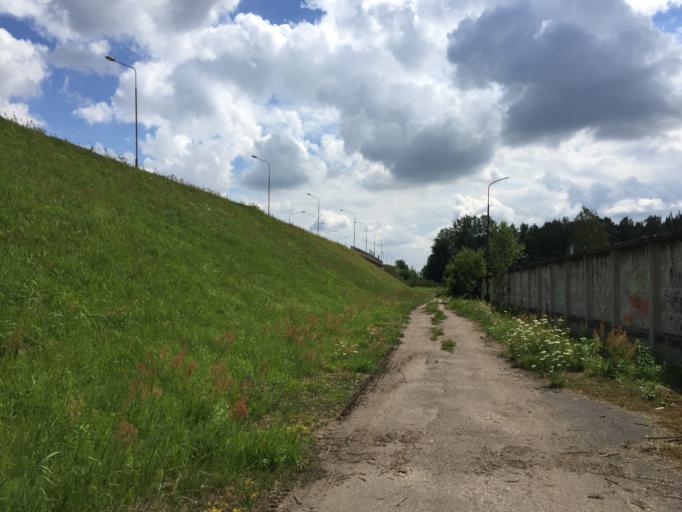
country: LV
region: Ozolnieku
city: Ozolnieki
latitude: 56.6644
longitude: 23.7765
